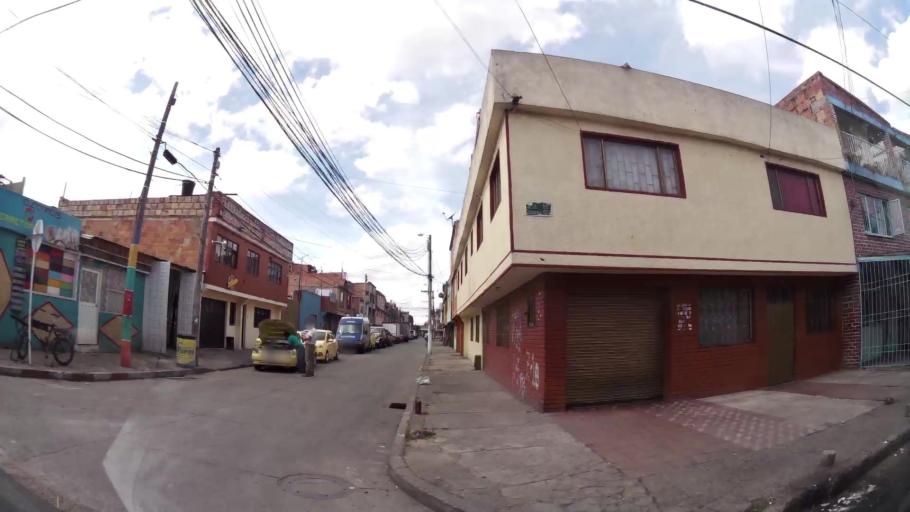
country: CO
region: Bogota D.C.
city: Bogota
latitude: 4.6951
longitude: -74.1132
